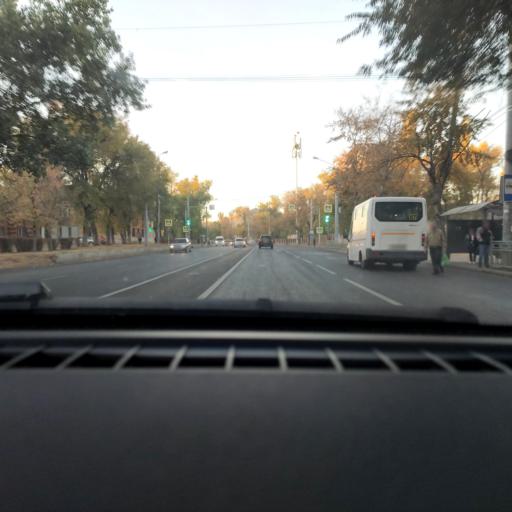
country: RU
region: Voronezj
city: Maslovka
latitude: 51.6157
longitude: 39.2479
